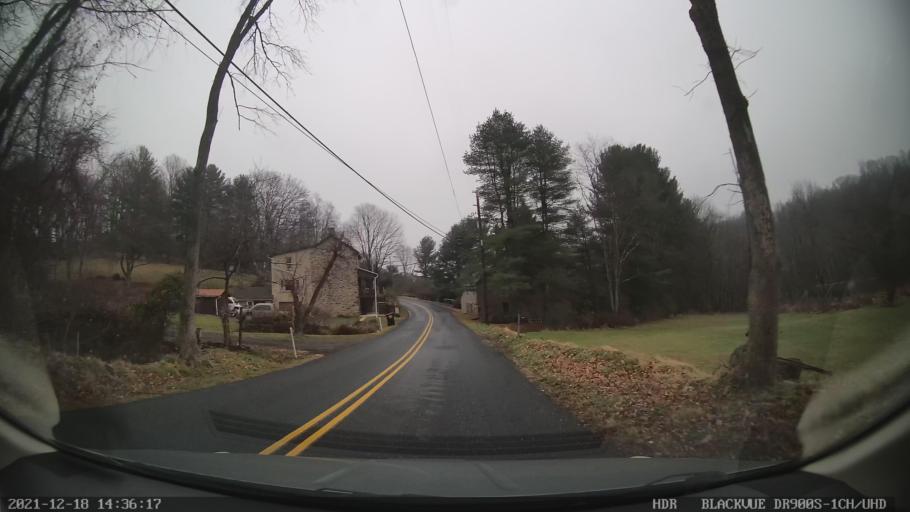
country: US
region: Pennsylvania
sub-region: Berks County
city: New Berlinville
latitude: 40.3858
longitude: -75.6519
